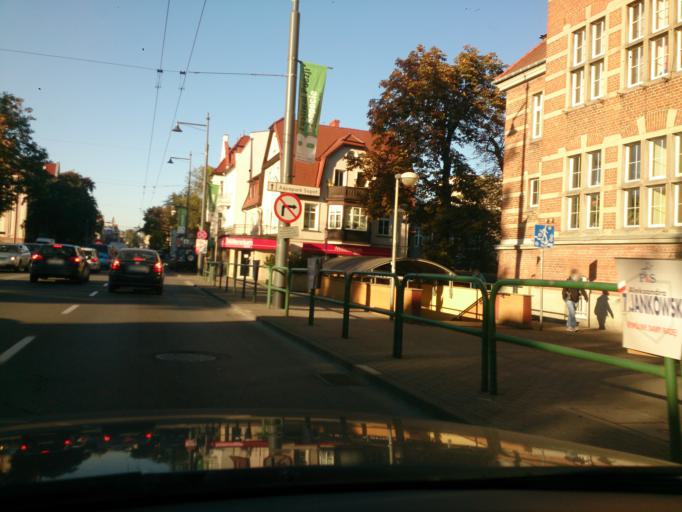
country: PL
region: Pomeranian Voivodeship
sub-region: Sopot
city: Sopot
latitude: 54.4388
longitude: 18.5608
